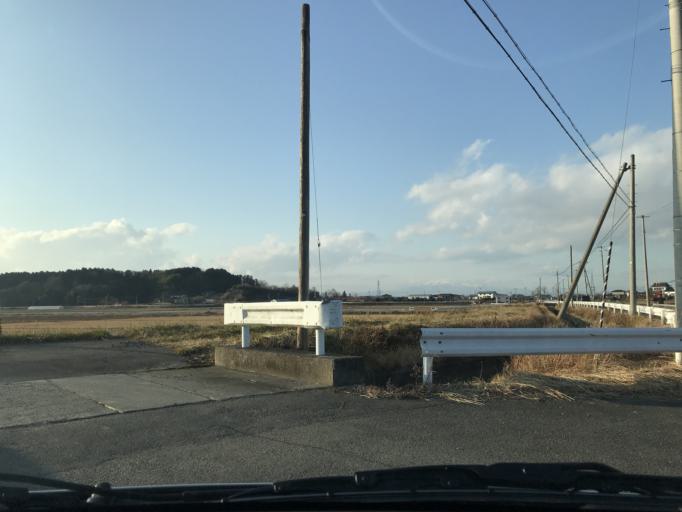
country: JP
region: Miyagi
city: Wakuya
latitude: 38.7166
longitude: 141.1445
